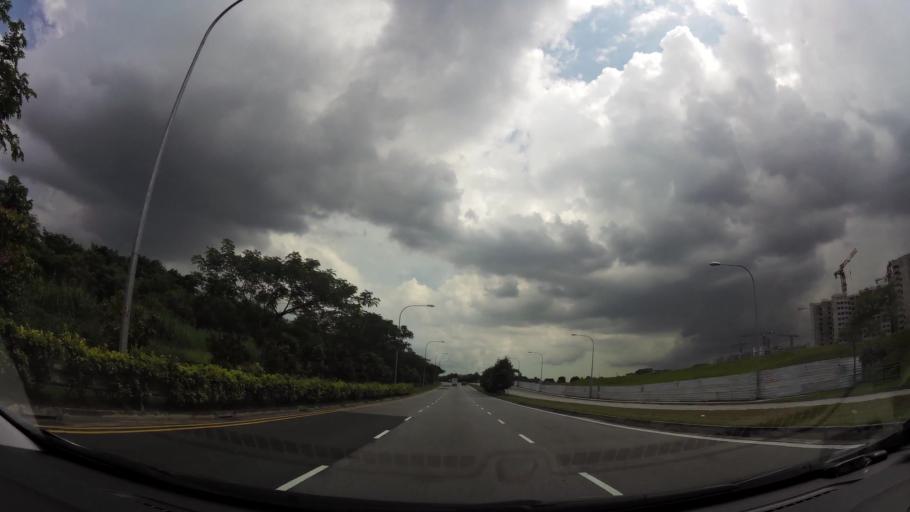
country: MY
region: Johor
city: Kampung Pasir Gudang Baru
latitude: 1.4304
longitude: 103.8514
